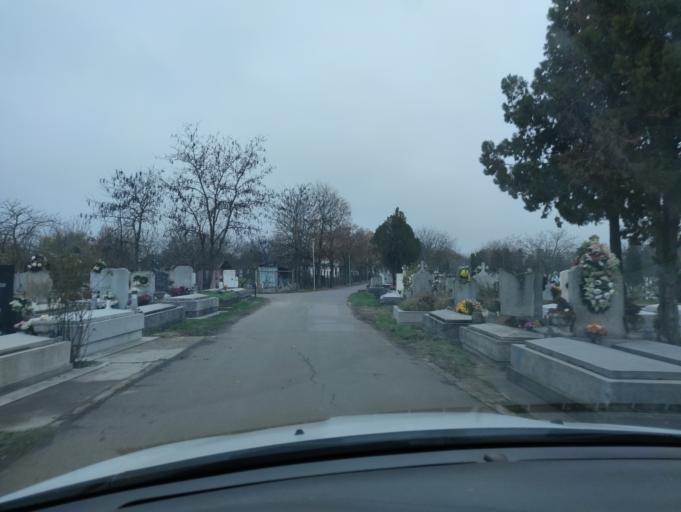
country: RO
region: Bihor
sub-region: Comuna Biharea
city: Oradea
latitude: 47.0391
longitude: 21.9249
